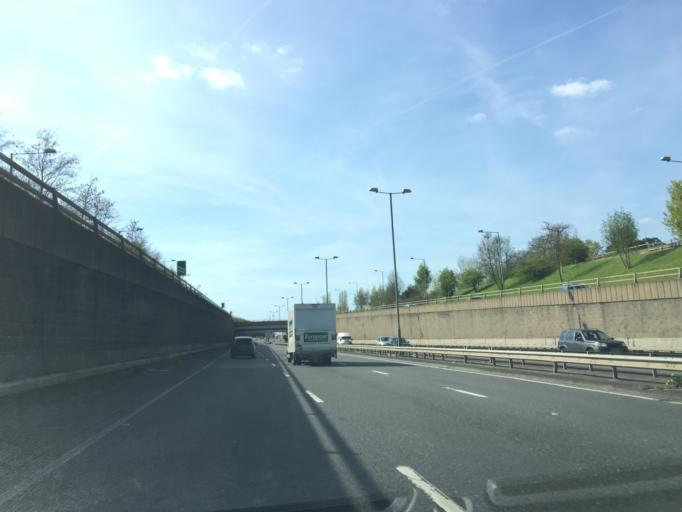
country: GB
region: England
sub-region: Greater London
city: Sidcup
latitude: 51.4171
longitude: 0.1010
